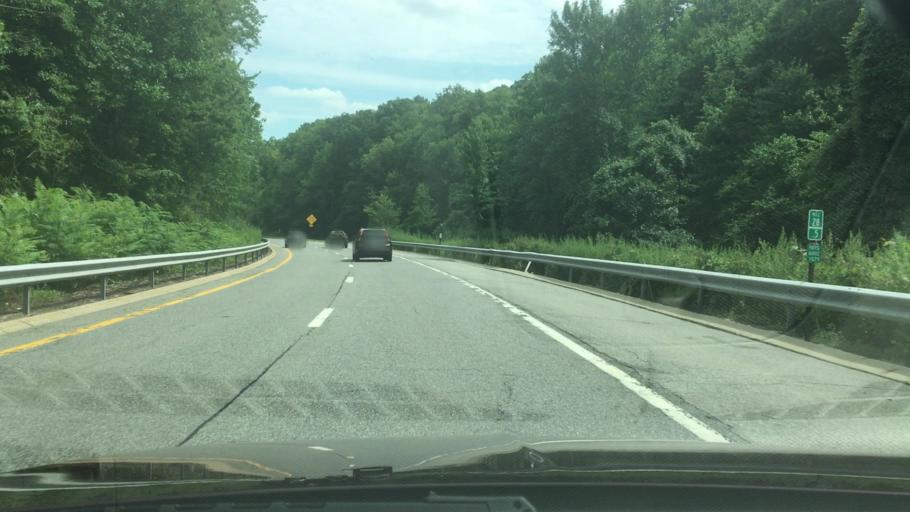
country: US
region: New York
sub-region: Putnam County
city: Mahopac
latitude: 41.4315
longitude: -73.8090
